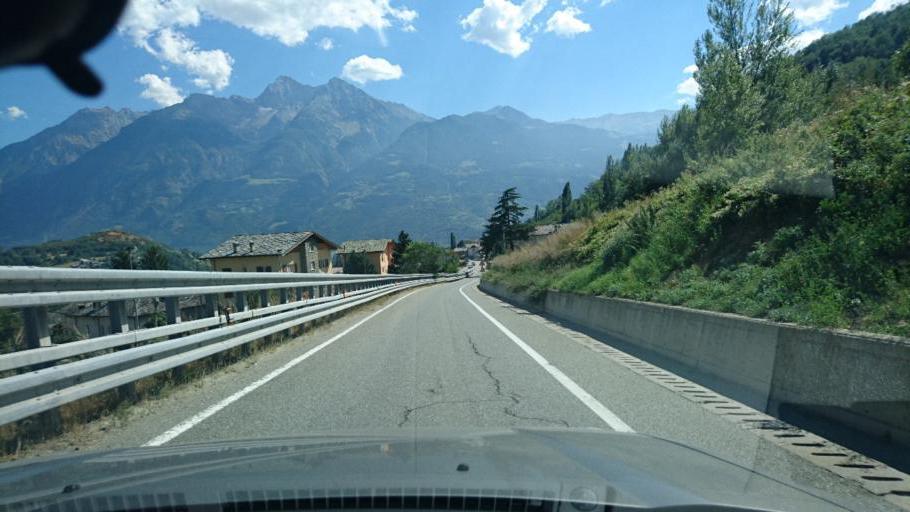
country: IT
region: Aosta Valley
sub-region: Valle d'Aosta
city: La Cretaz-Roisan
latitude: 45.7618
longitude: 7.3144
